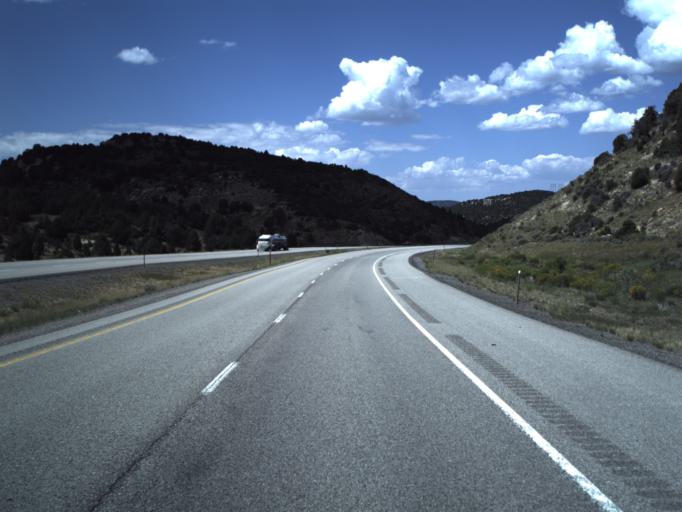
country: US
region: Utah
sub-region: Sevier County
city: Salina
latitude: 38.7883
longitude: -111.5017
